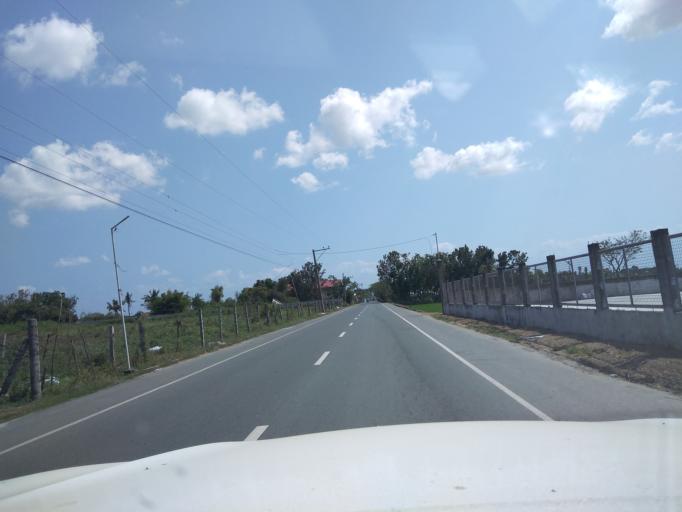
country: PH
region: Central Luzon
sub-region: Province of Pampanga
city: Bahay Pare
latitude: 15.0419
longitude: 120.8793
